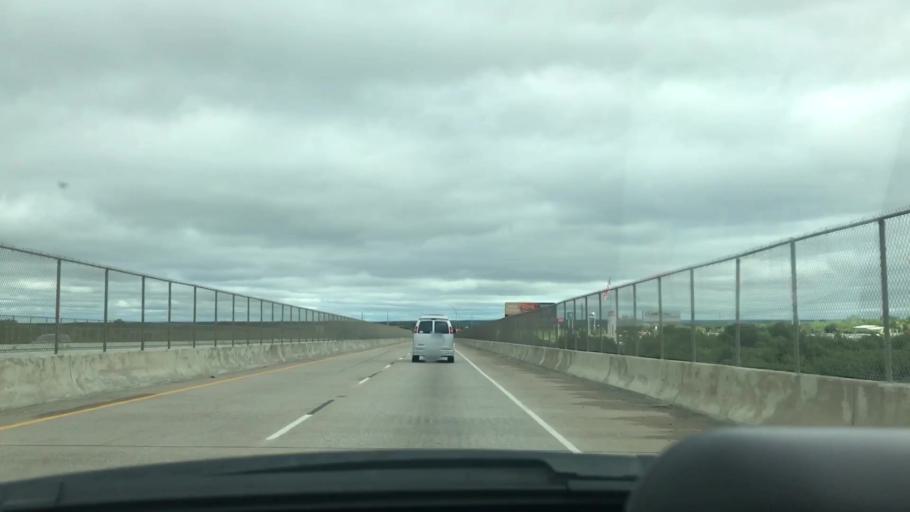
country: US
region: Texas
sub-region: Grayson County
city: Denison
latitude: 33.7703
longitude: -96.5848
